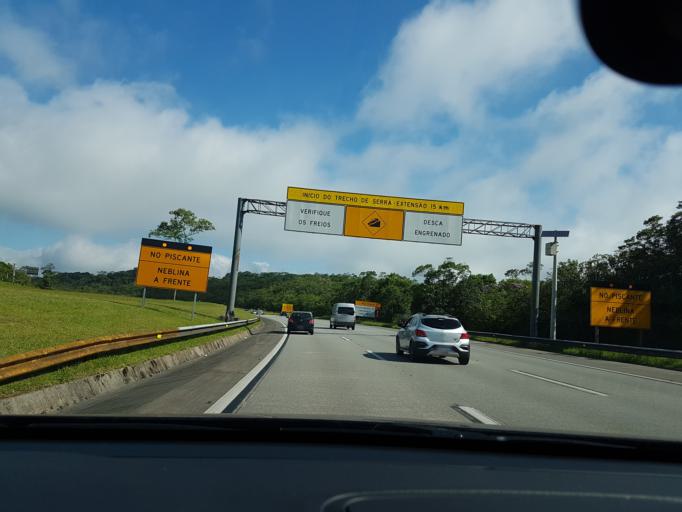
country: BR
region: Sao Paulo
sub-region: Cubatao
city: Cubatao
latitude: -23.9244
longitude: -46.5551
